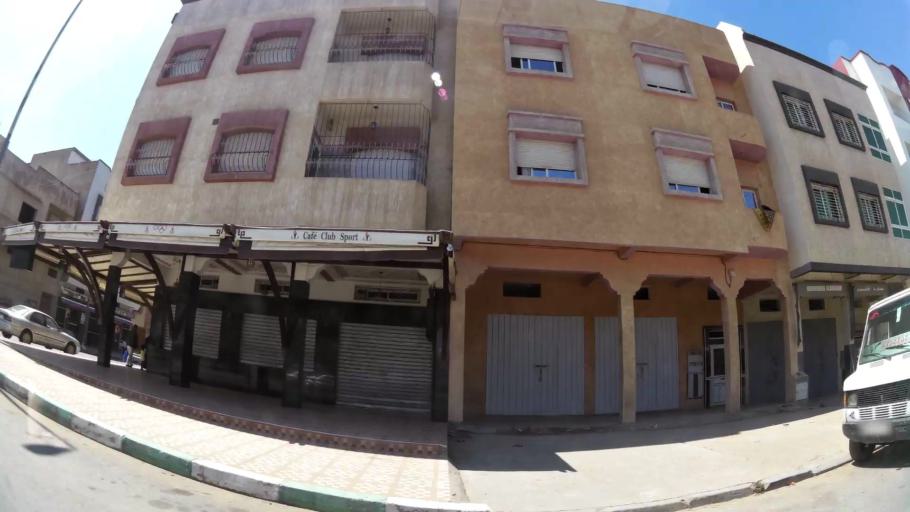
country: MA
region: Gharb-Chrarda-Beni Hssen
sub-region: Kenitra Province
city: Kenitra
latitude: 34.2444
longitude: -6.5416
